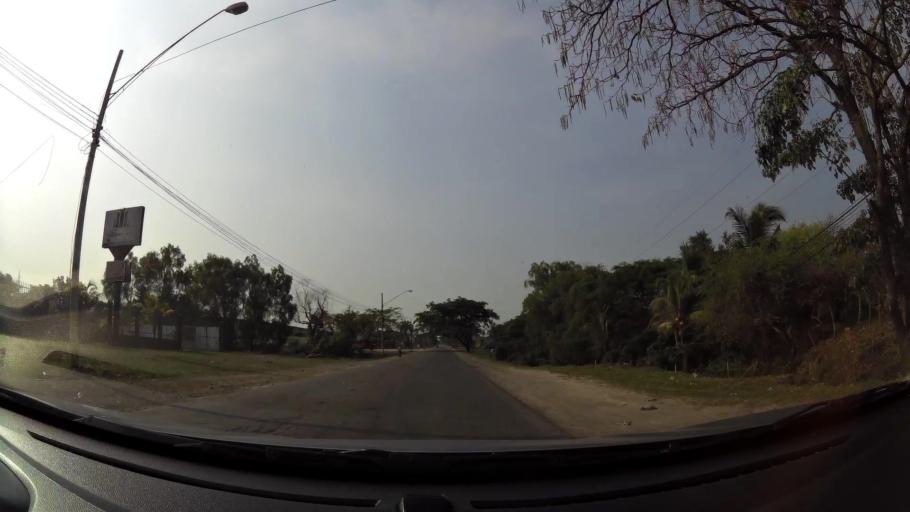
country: HN
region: Comayagua
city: Comayagua
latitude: 14.4371
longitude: -87.6340
